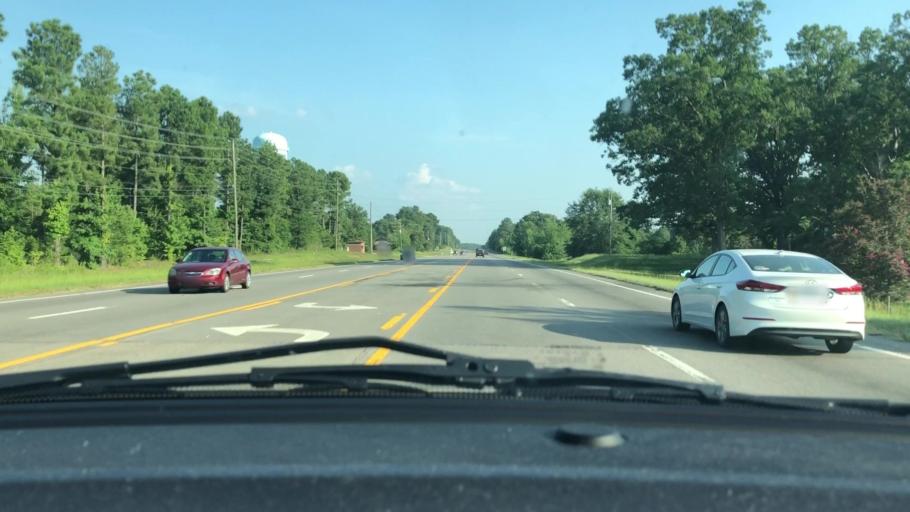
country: US
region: North Carolina
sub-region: Lee County
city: Broadway
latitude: 35.4194
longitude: -79.1187
